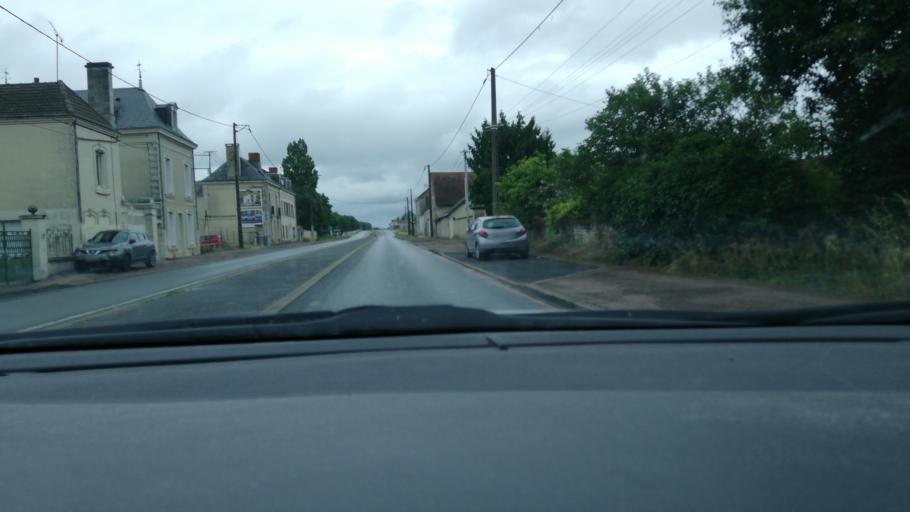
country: FR
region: Poitou-Charentes
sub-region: Departement de la Vienne
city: Naintre
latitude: 46.7645
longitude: 0.4966
